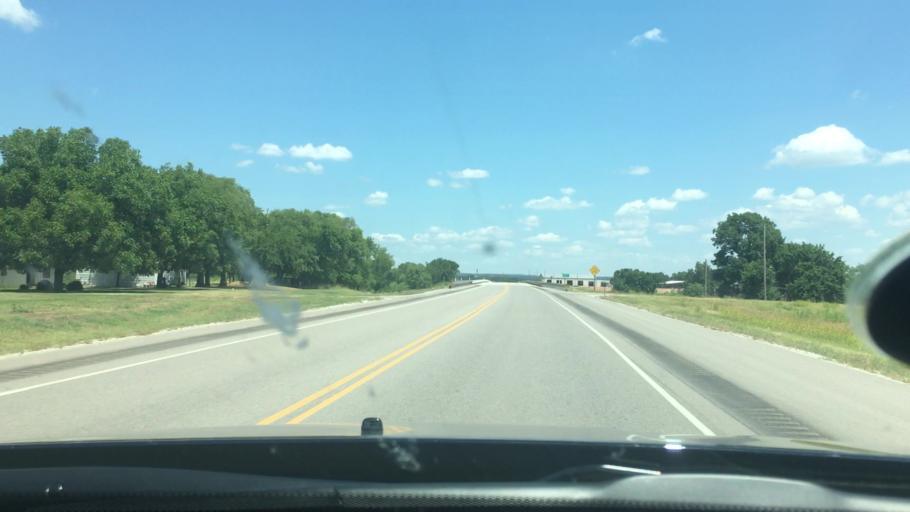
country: US
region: Oklahoma
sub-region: Carter County
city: Dickson
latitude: 34.2317
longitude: -96.9764
